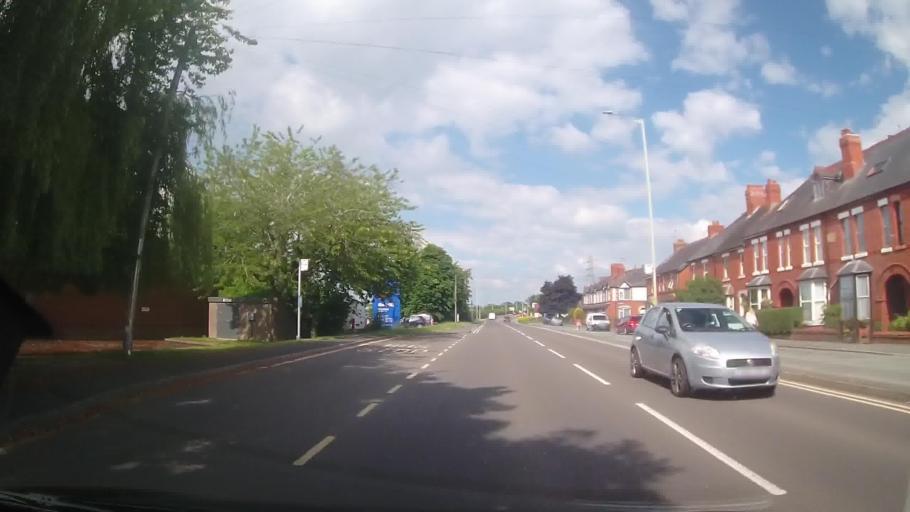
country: GB
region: England
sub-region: Shropshire
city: Oswestry
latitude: 52.8669
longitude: -3.0411
